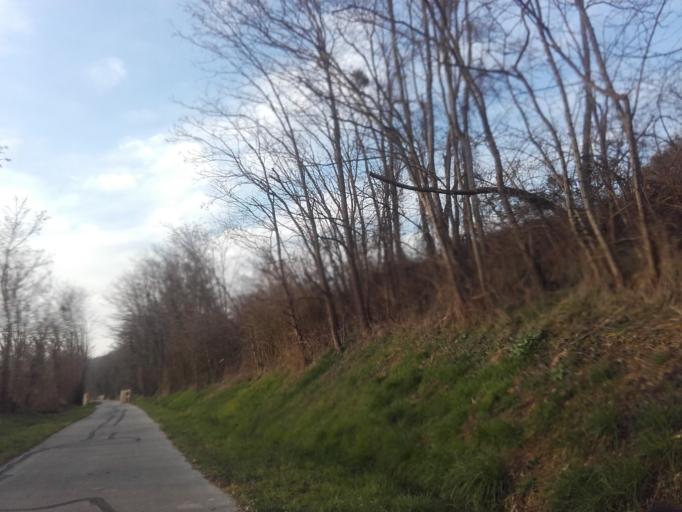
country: FR
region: Bourgogne
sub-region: Departement de la Cote-d'Or
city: Nolay
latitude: 46.9051
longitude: 4.6621
